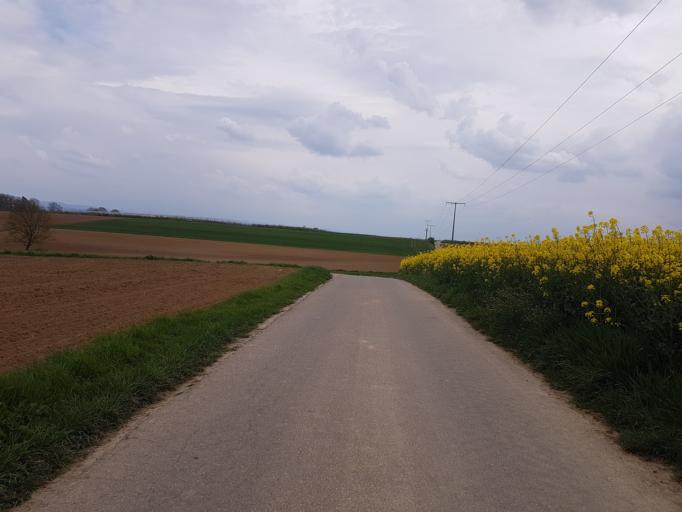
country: DE
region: Baden-Wuerttemberg
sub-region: Regierungsbezirk Stuttgart
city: Bondorf
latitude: 48.5371
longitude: 8.8217
